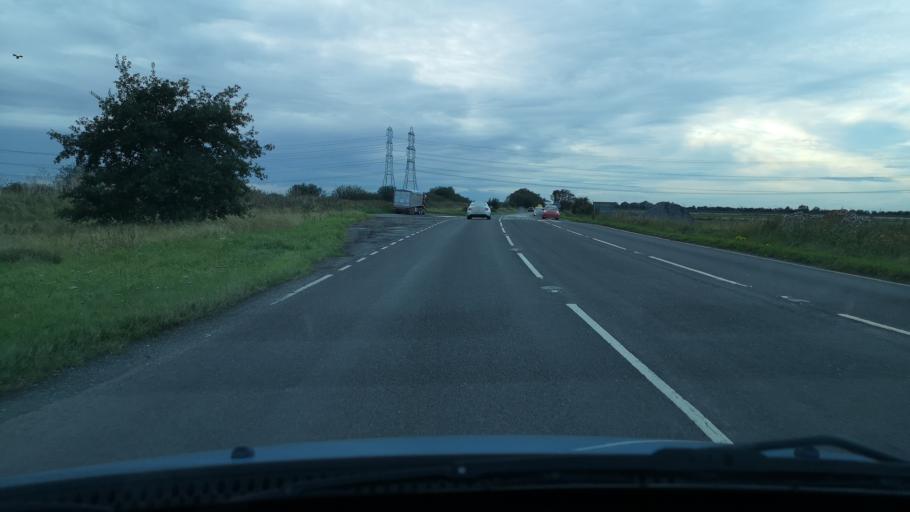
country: GB
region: England
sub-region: North Lincolnshire
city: Gunness
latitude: 53.5767
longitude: -0.7544
